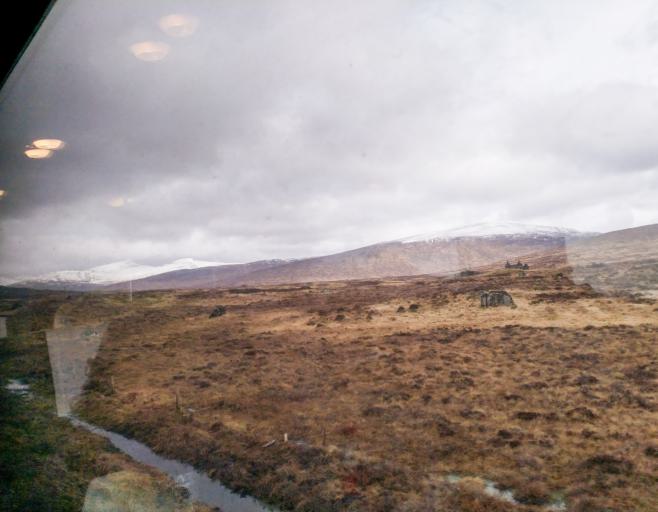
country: GB
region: Scotland
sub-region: Highland
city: Spean Bridge
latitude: 56.7388
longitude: -4.6615
